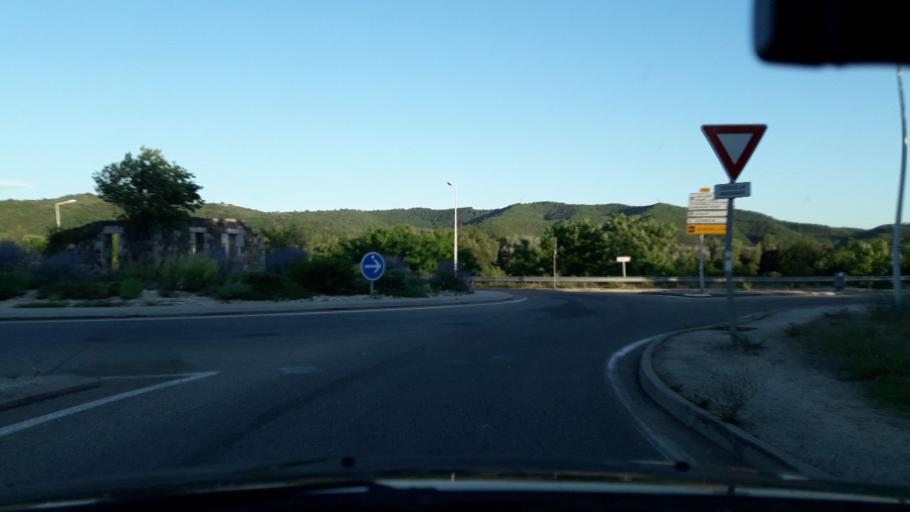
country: FR
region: Rhone-Alpes
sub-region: Departement de l'Ardeche
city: Lavilledieu
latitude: 44.5678
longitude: 4.4617
